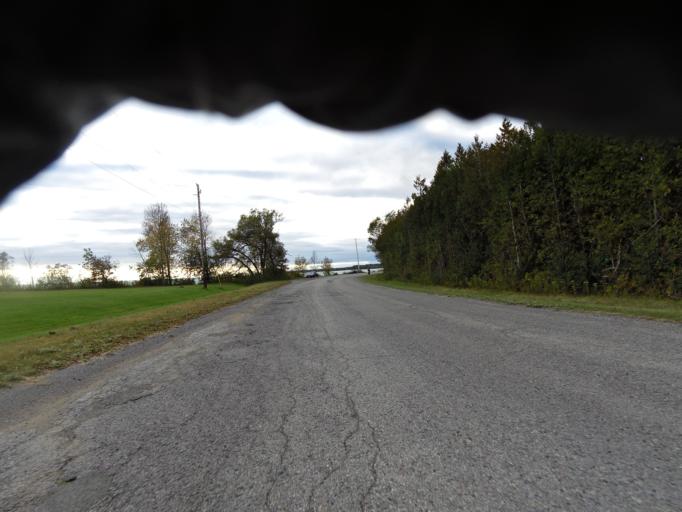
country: CA
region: Ontario
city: Cobourg
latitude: 43.9755
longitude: -77.9585
